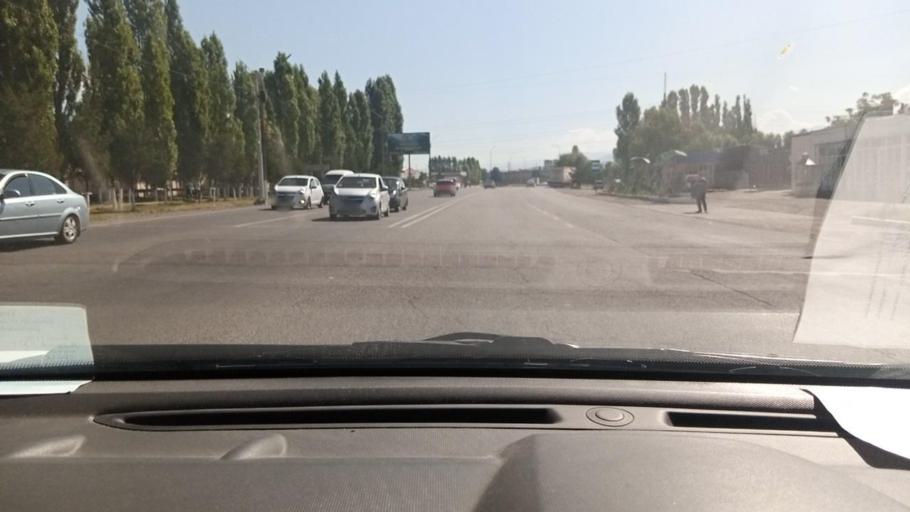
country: UZ
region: Toshkent
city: Angren
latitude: 40.9914
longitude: 70.0436
